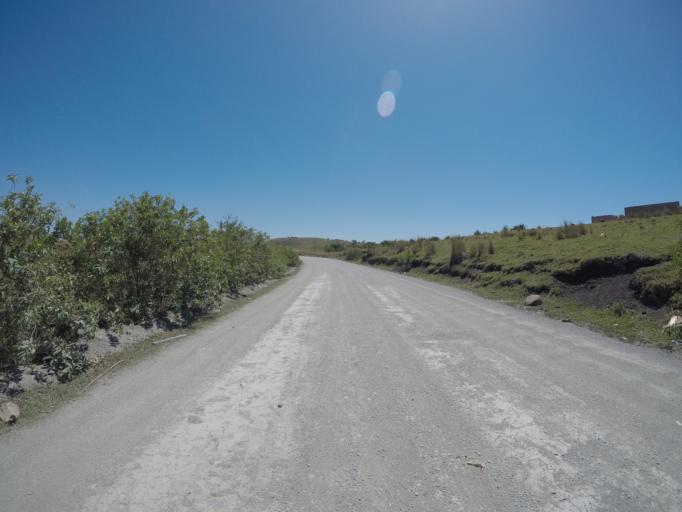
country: ZA
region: Eastern Cape
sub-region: OR Tambo District Municipality
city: Libode
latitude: -31.9950
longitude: 29.0591
